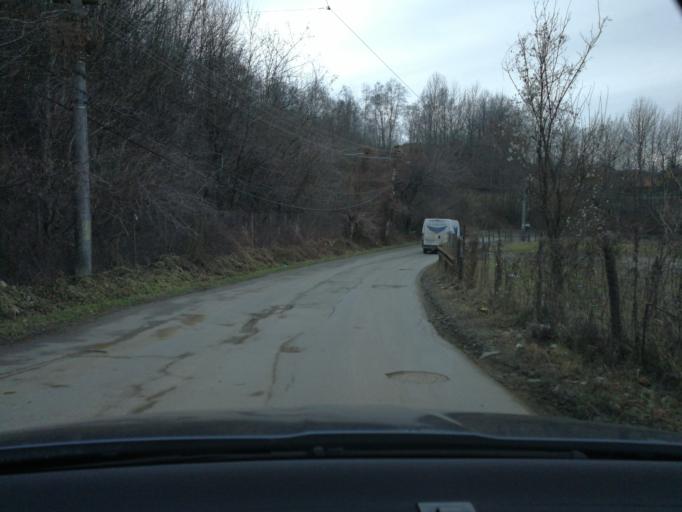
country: RO
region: Prahova
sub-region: Oras Breaza
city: Breaza
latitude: 45.1802
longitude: 25.6516
